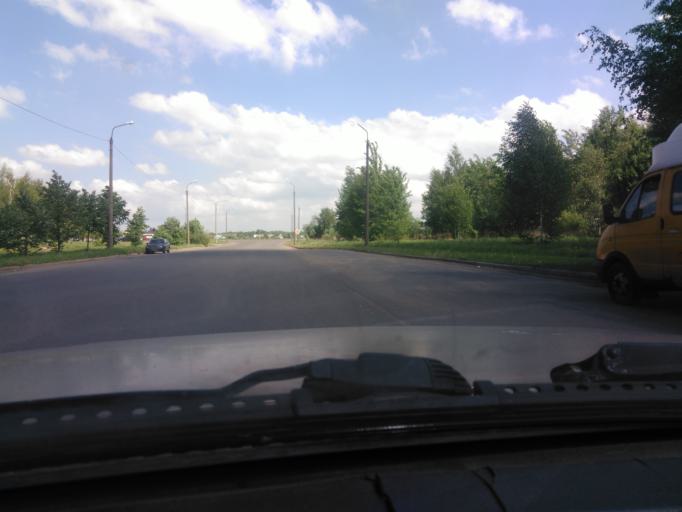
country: BY
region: Mogilev
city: Palykavichy Pyershyya
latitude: 53.9477
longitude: 30.3736
